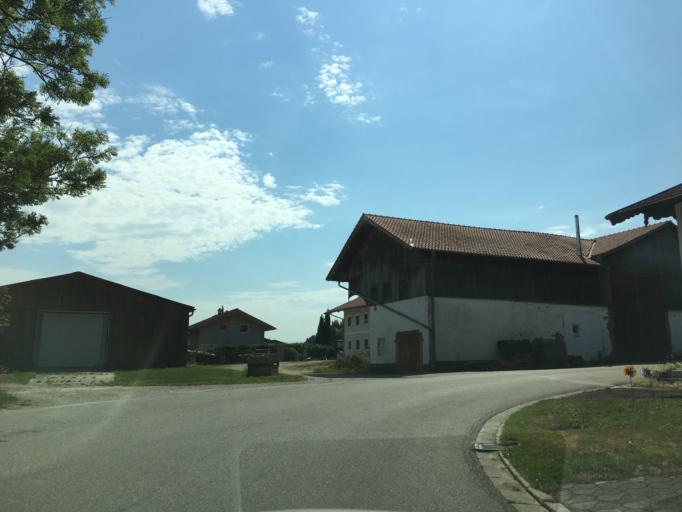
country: DE
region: Bavaria
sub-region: Upper Bavaria
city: Steinhoring
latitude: 48.1158
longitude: 12.0667
